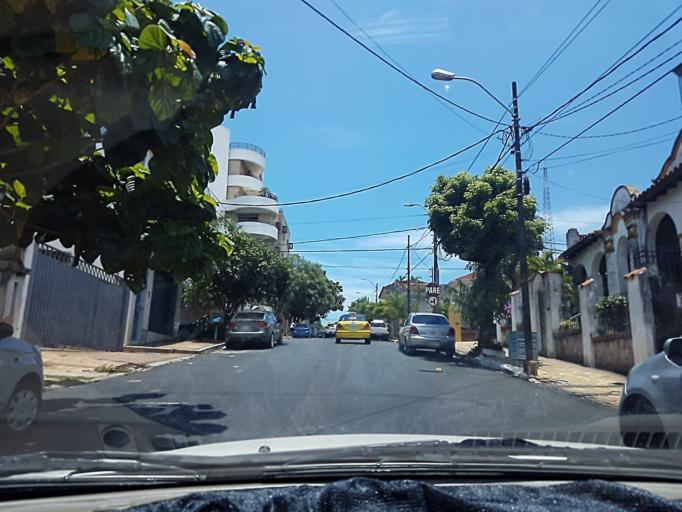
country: PY
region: Asuncion
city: Asuncion
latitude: -25.2908
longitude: -57.6360
